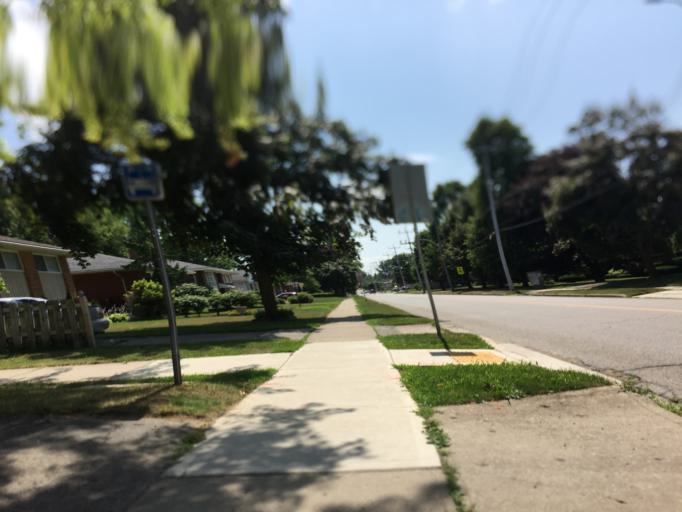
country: CA
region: Ontario
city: Stratford
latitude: 43.3805
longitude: -80.9962
